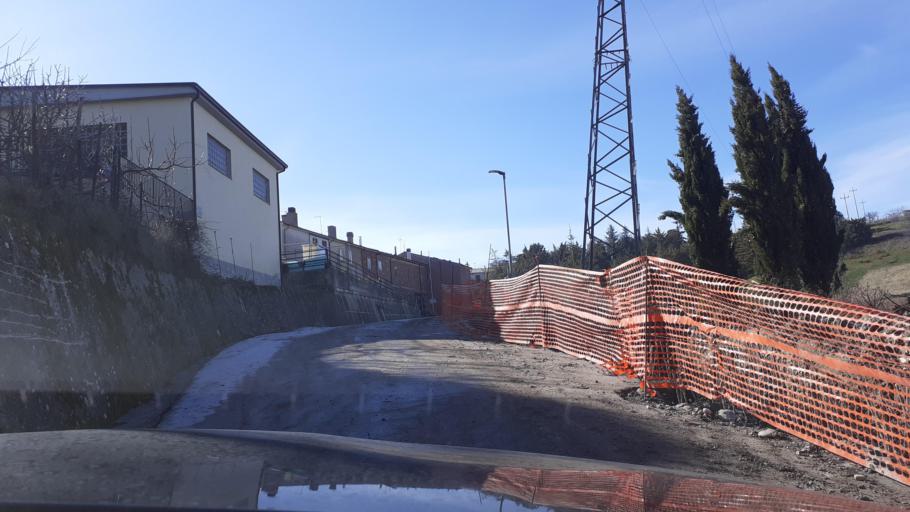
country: IT
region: Molise
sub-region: Provincia di Campobasso
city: Pietracupa
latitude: 41.6832
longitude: 14.5196
